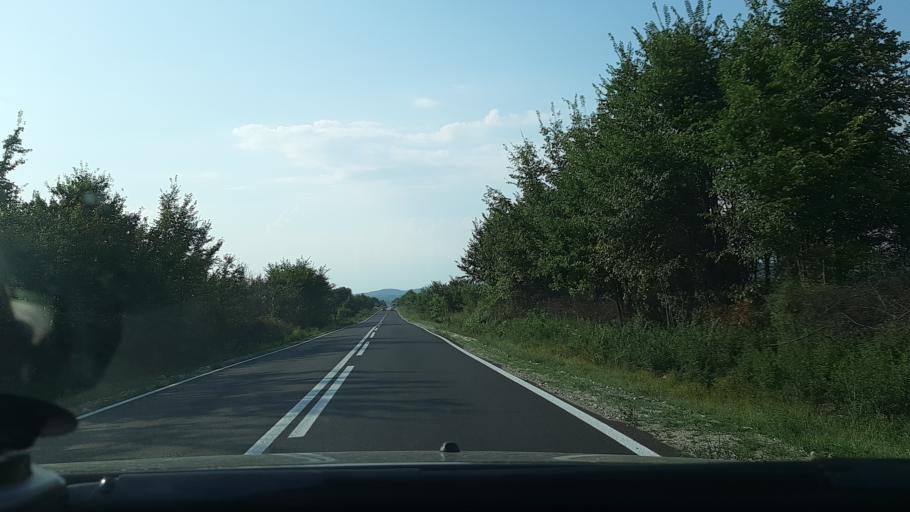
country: RO
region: Gorj
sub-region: Comuna Targu Carbunesti
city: Pojogeni
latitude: 45.0020
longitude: 23.4900
